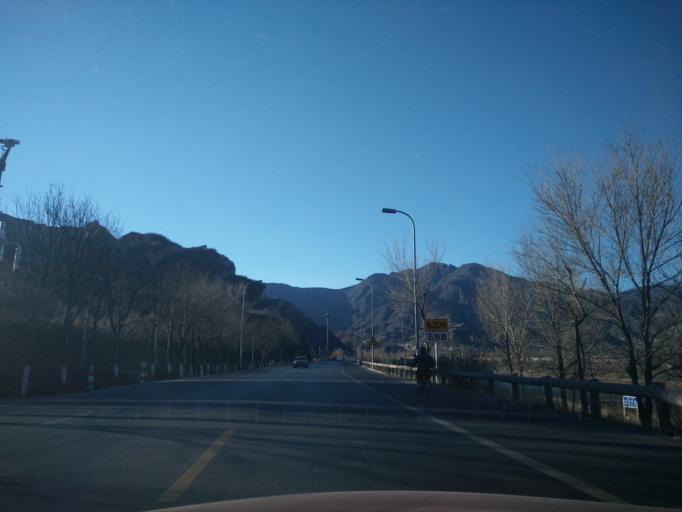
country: CN
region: Beijing
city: Miaofengshan
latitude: 39.9830
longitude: 116.0609
